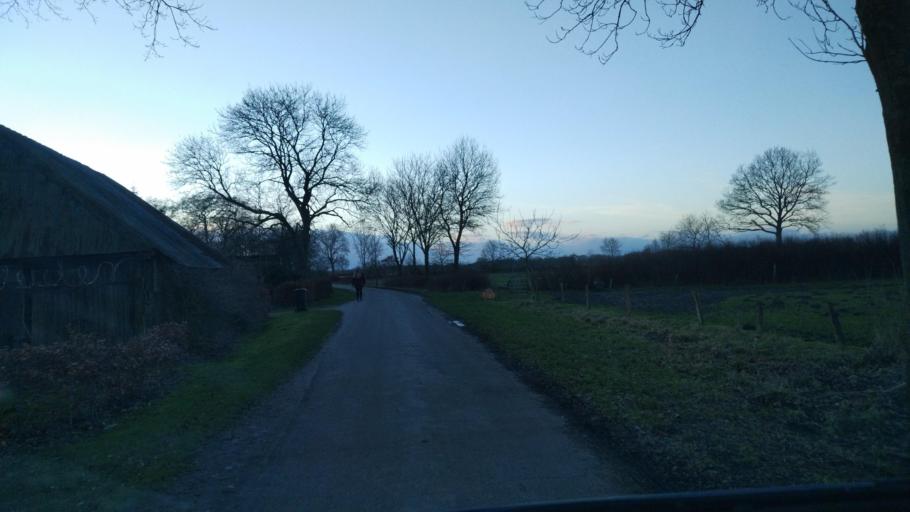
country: DE
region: Schleswig-Holstein
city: Gross Rheide
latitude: 54.4421
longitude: 9.4097
